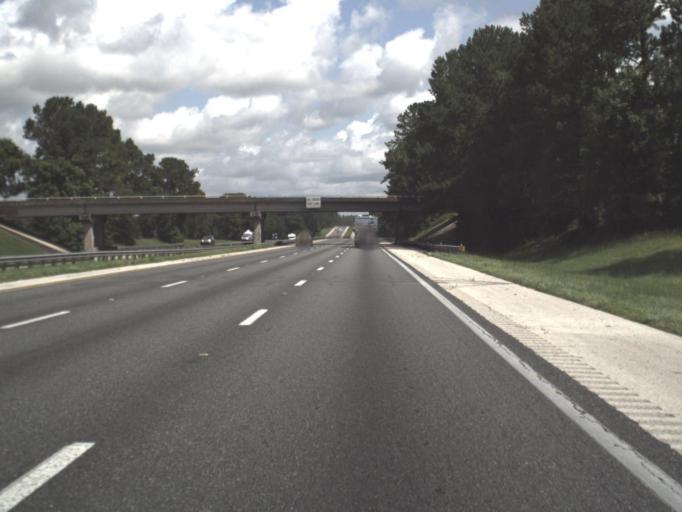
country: US
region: Florida
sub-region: Alachua County
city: High Springs
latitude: 29.8377
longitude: -82.5272
